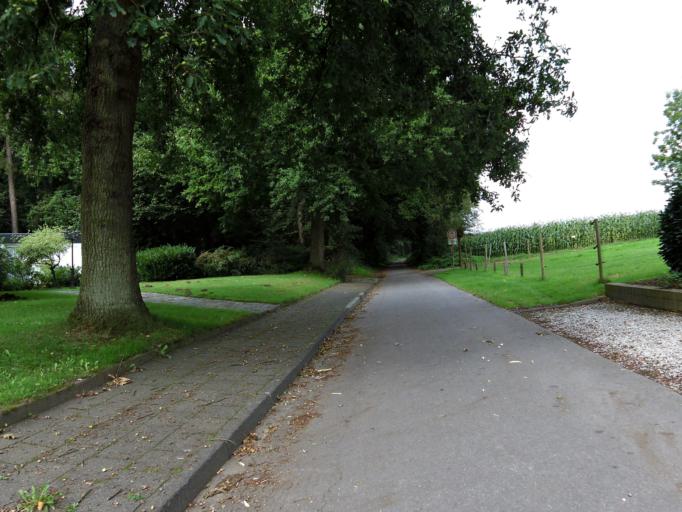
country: NL
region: Limburg
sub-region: Gemeente Onderbanken
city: Schinveld
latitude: 50.9845
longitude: 5.9762
